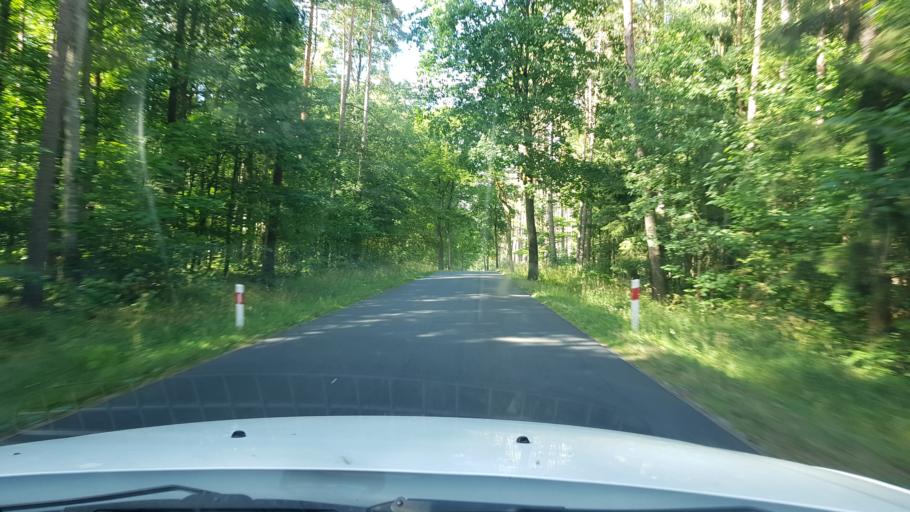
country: PL
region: West Pomeranian Voivodeship
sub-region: Powiat drawski
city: Zlocieniec
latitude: 53.5718
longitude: 16.0096
